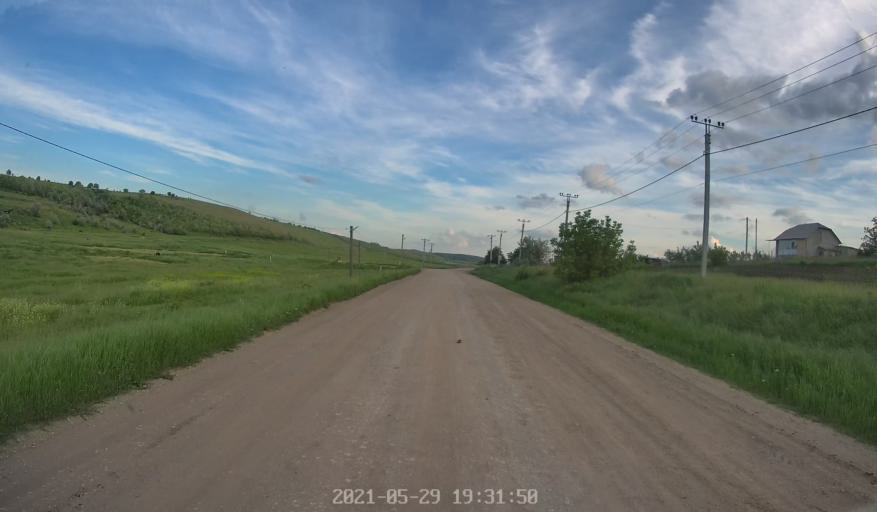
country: MD
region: Chisinau
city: Singera
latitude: 46.8344
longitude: 28.9558
